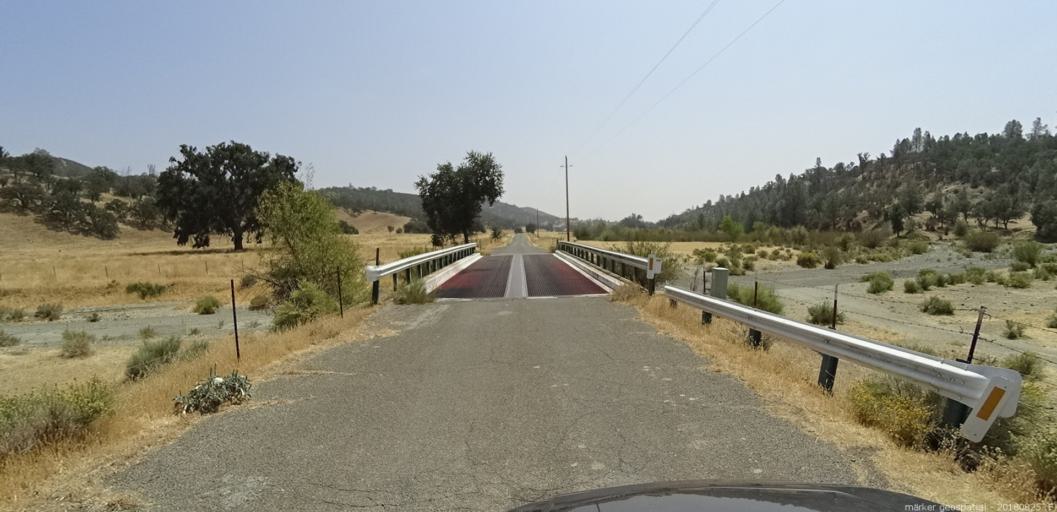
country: US
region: California
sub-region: Fresno County
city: Coalinga
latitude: 35.9464
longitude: -120.4698
